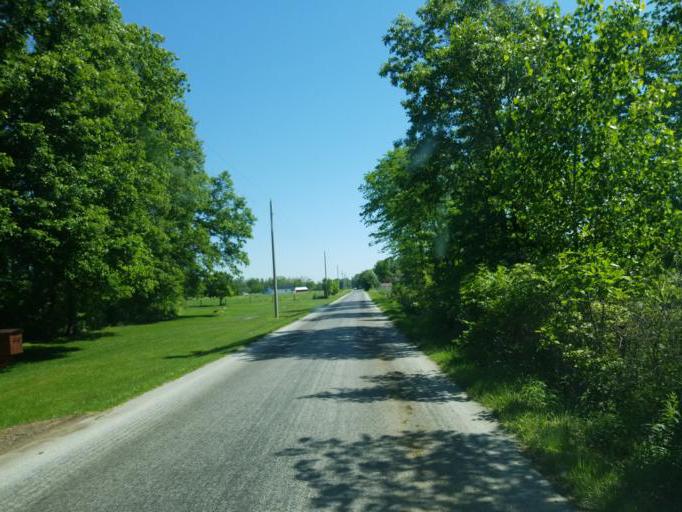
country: US
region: Ohio
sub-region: Hardin County
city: Kenton
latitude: 40.6138
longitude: -83.5055
